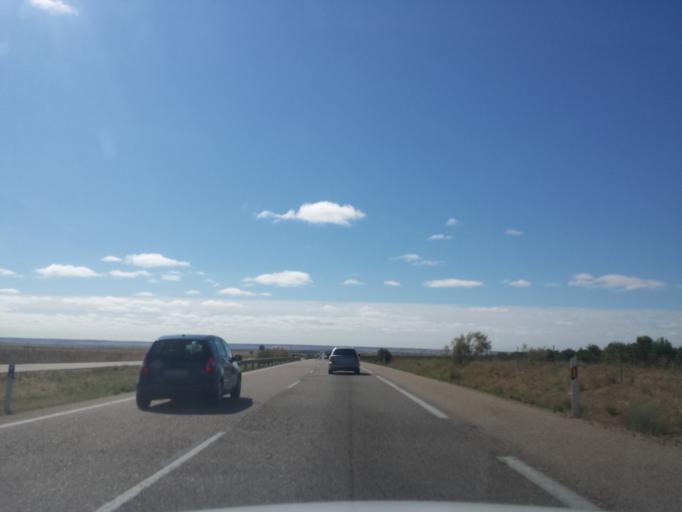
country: ES
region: Castille and Leon
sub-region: Provincia de Zamora
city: Quintanilla del Monte
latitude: 41.8213
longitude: -5.3710
